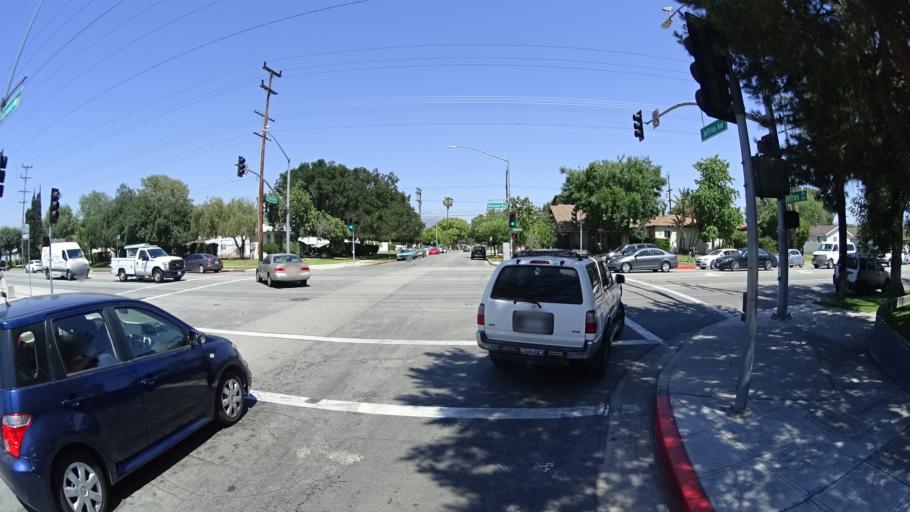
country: US
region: California
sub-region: Los Angeles County
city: North Hollywood
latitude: 34.1810
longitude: -118.3497
